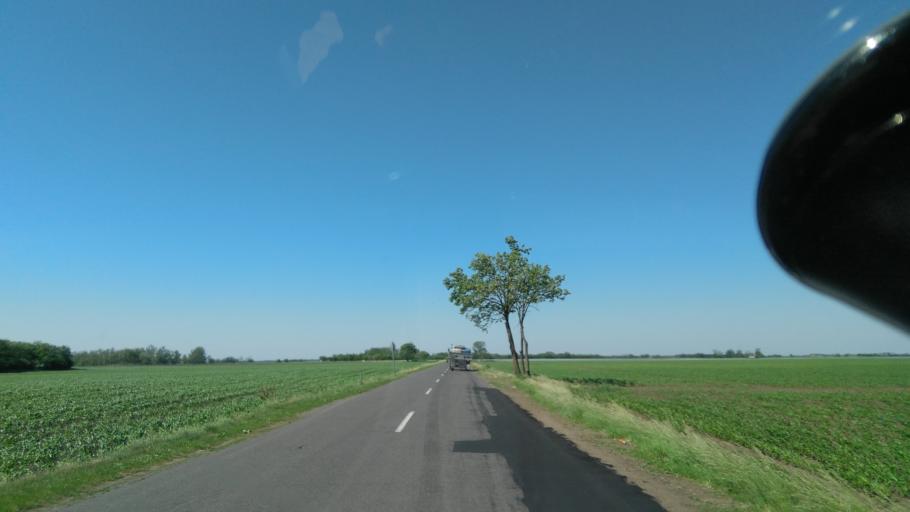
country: HU
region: Bekes
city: Kevermes
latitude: 46.4345
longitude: 21.1727
